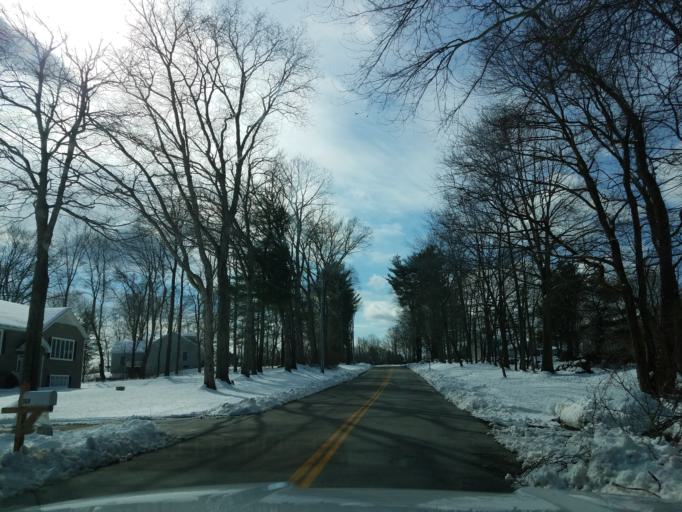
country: US
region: Connecticut
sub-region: New London County
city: Colchester
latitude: 41.5914
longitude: -72.3512
